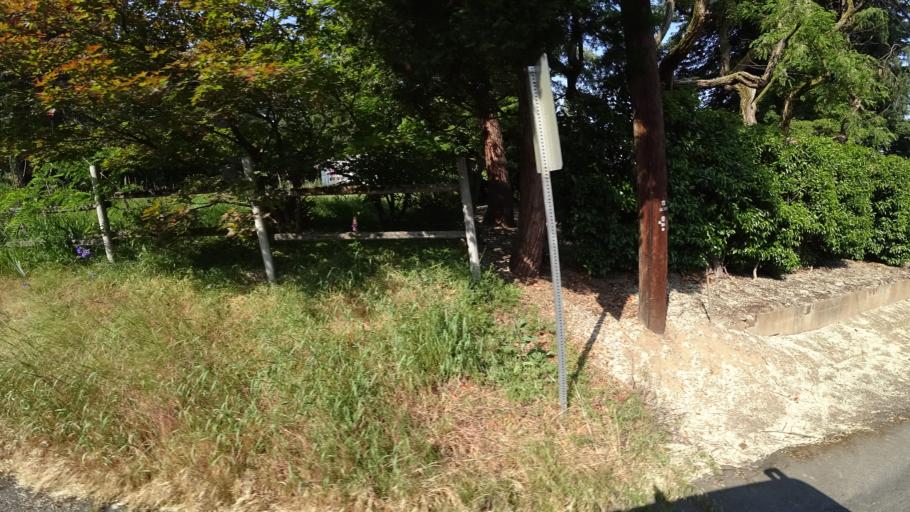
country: US
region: Oregon
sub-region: Clackamas County
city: Happy Valley
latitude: 45.4512
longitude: -122.5375
